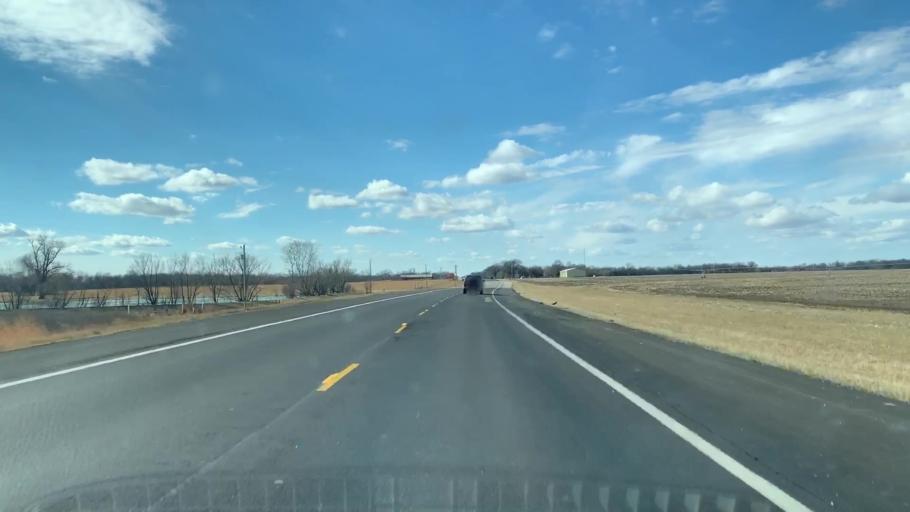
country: US
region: Kansas
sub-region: Labette County
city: Parsons
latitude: 37.3403
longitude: -95.1203
